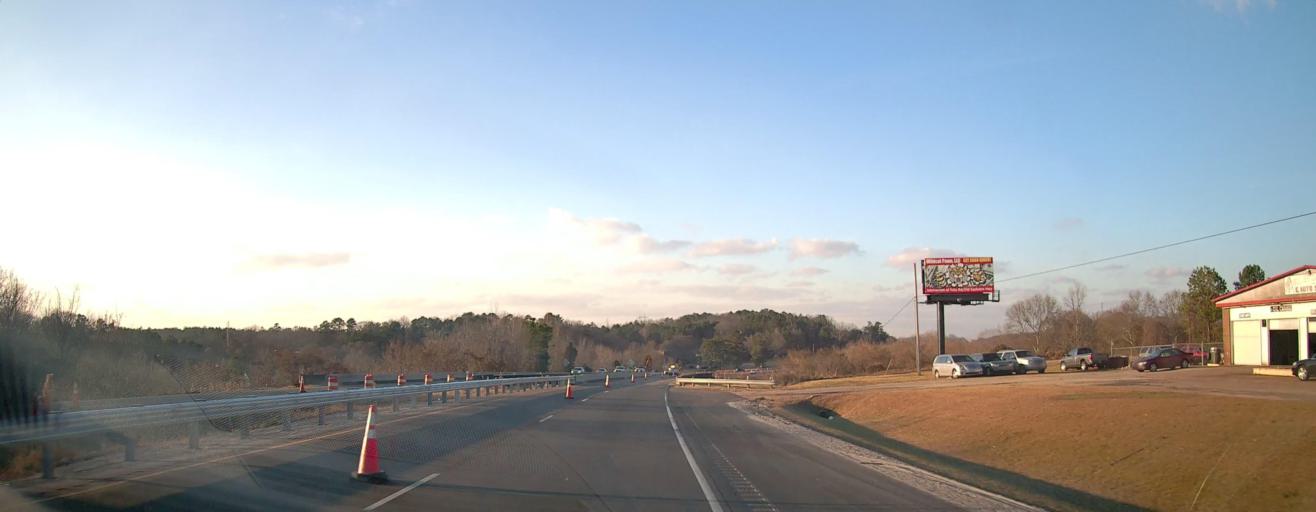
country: US
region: Alabama
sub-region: Calhoun County
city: Saks
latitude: 33.7212
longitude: -85.8742
